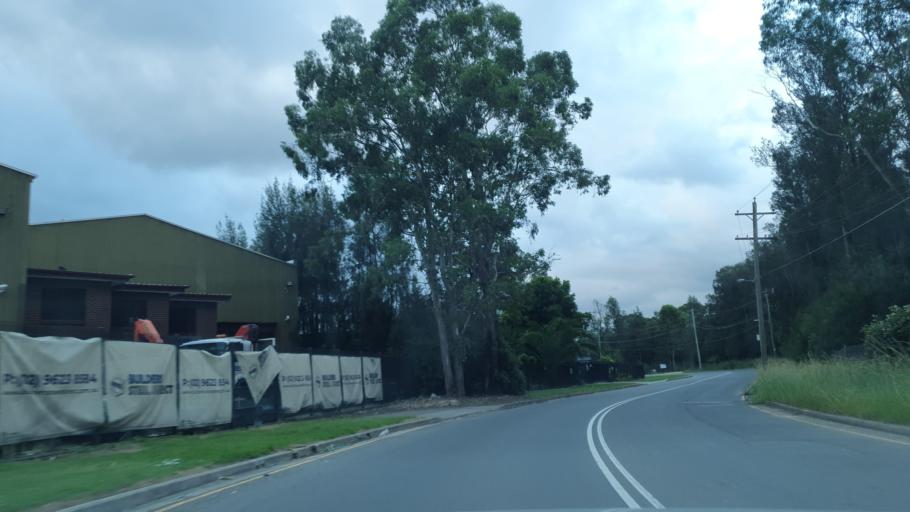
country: AU
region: New South Wales
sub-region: Penrith Municipality
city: Werrington County
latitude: -33.7408
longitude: 150.7745
